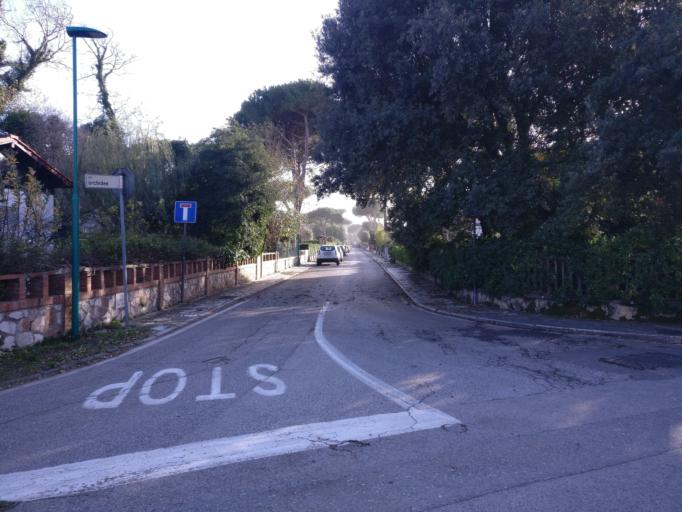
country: IT
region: Tuscany
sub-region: Province of Pisa
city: Marina di Pisa-Tirrenia-Calambrone
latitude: 43.6131
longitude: 10.2932
